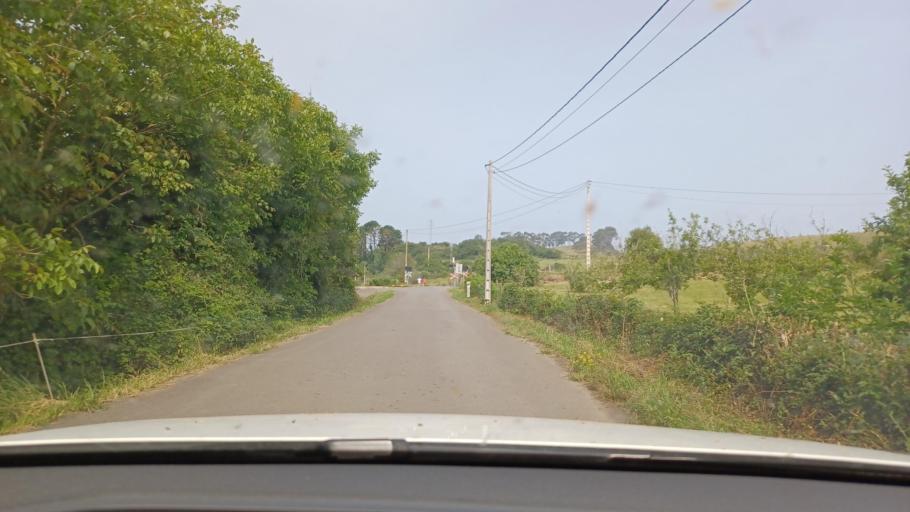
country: ES
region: Asturias
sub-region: Province of Asturias
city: Ribadesella
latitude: 43.4578
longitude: -5.0395
